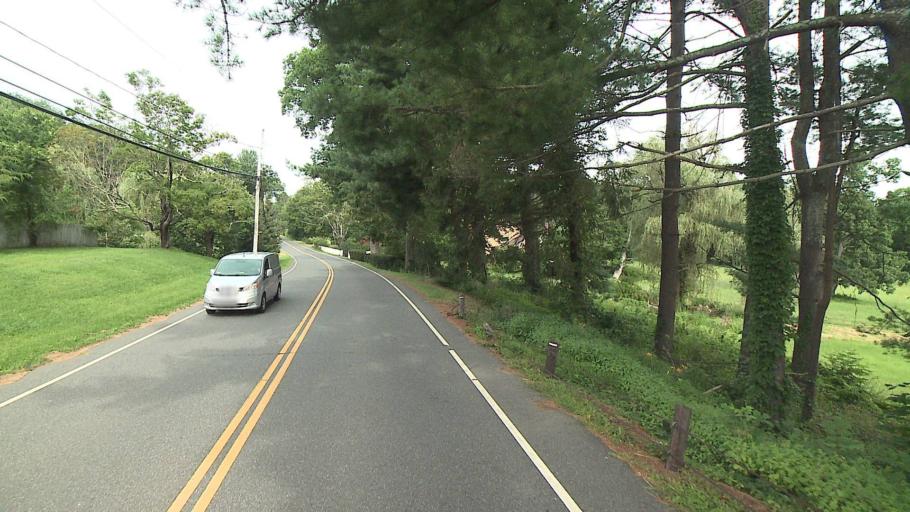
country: US
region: Connecticut
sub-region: Litchfield County
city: Woodbury
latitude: 41.5689
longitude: -73.2218
